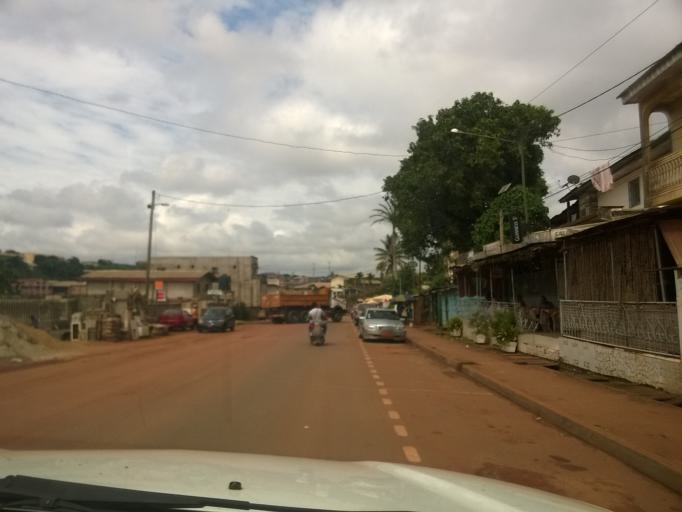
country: CM
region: Centre
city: Yaounde
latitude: 3.8671
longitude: 11.5352
